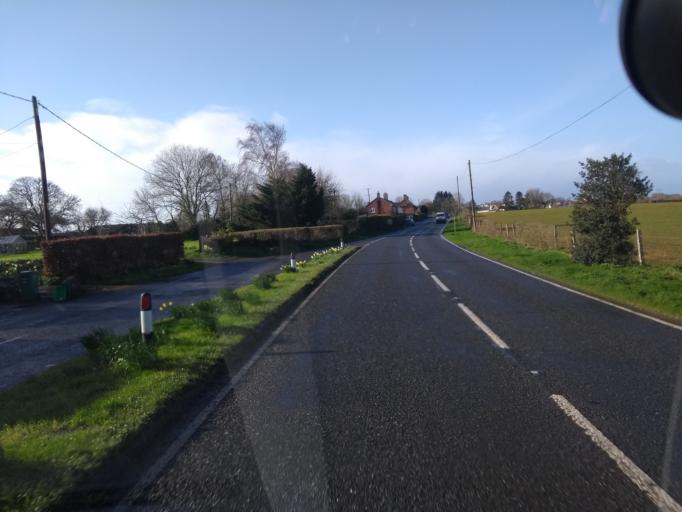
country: GB
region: England
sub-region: Somerset
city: Yeovil
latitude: 50.9707
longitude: -2.6119
